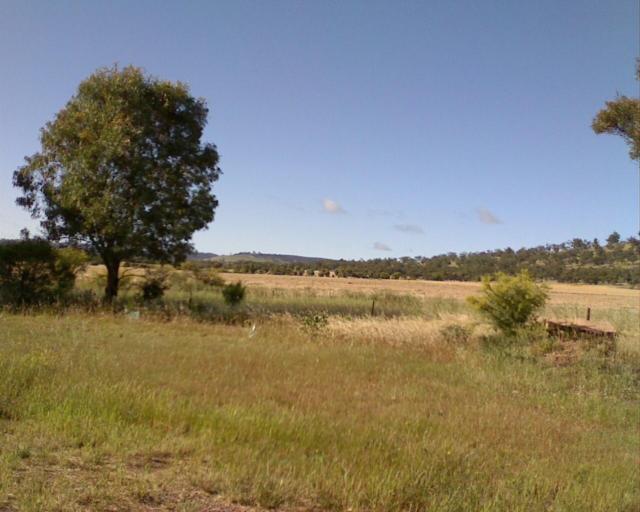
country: AU
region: South Australia
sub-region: Flinders Ranges
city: Quorn
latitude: -32.6493
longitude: 138.0934
